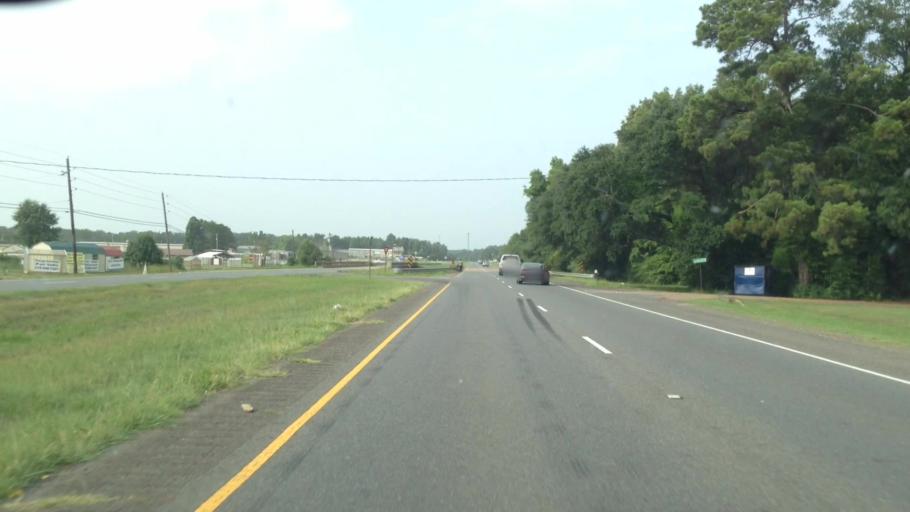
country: US
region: Louisiana
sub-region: De Soto Parish
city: Stonewall
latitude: 32.3701
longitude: -93.8239
